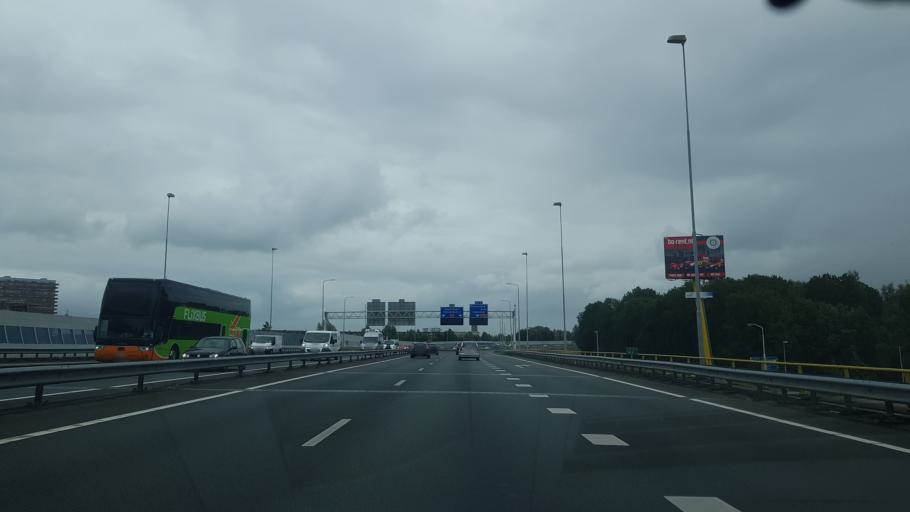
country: NL
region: North Holland
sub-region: Gemeente Beemster
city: Halfweg
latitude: 52.5114
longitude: 4.9332
